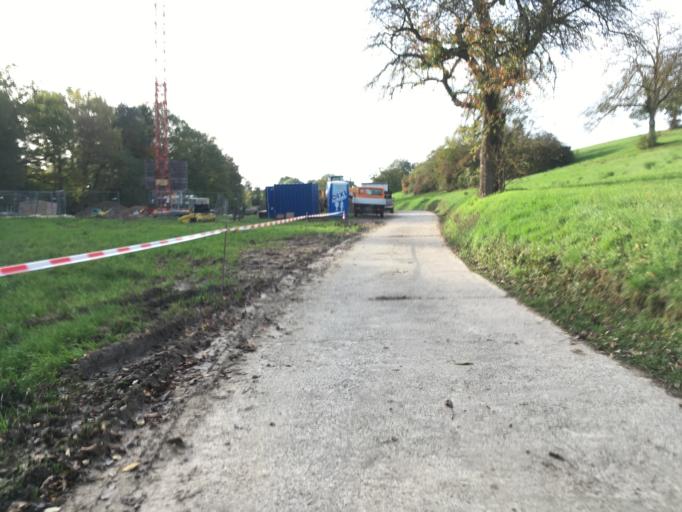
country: DE
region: Baden-Wuerttemberg
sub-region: Karlsruhe Region
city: Zuzenhausen
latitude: 49.2704
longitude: 8.8281
